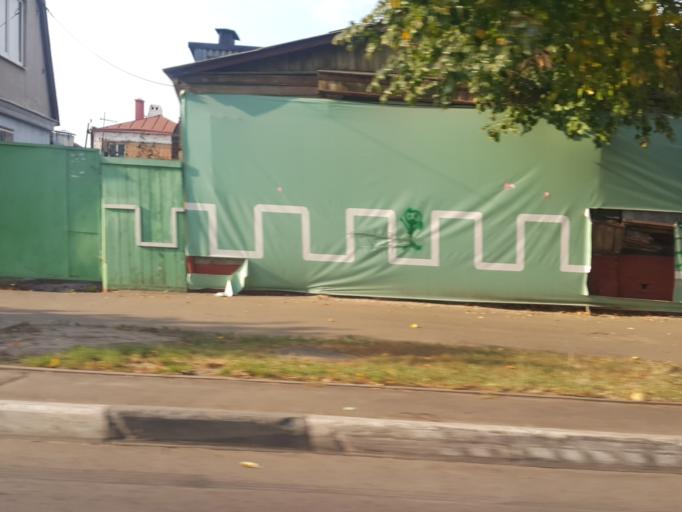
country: RU
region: Tambov
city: Tambov
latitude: 52.7086
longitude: 41.4609
